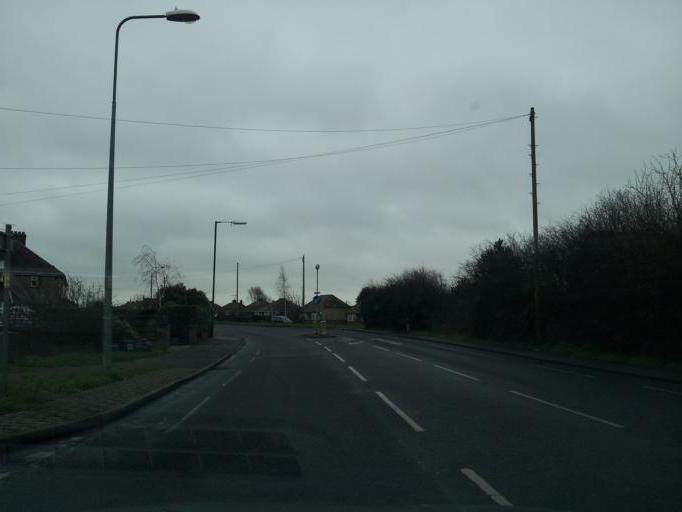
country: GB
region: England
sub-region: Essex
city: Dovercourt
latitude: 51.9292
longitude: 1.2352
